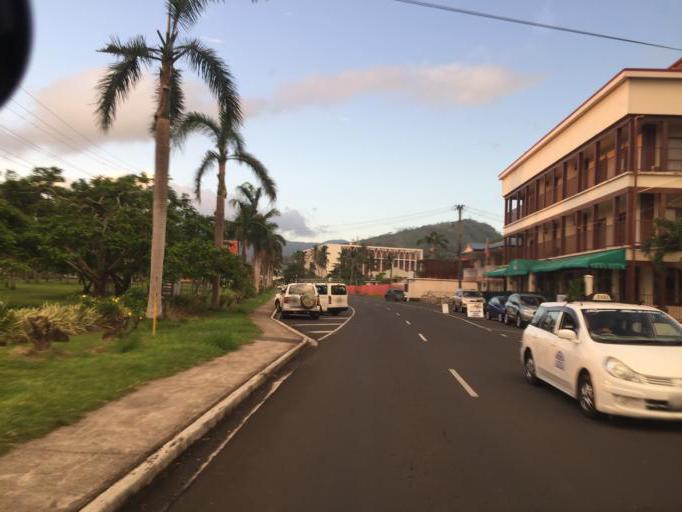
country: WS
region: Tuamasaga
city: Apia
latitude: -13.8256
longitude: -171.7733
